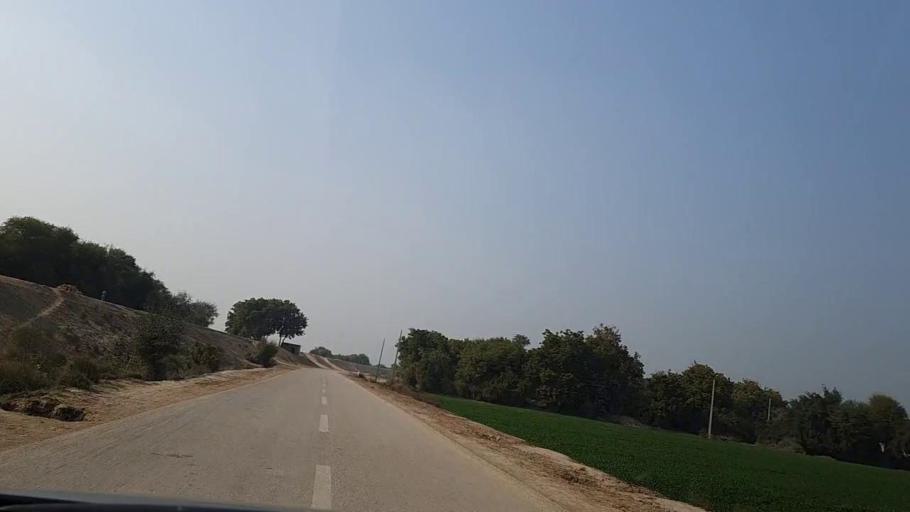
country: PK
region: Sindh
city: Sann
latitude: 26.1522
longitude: 68.1226
